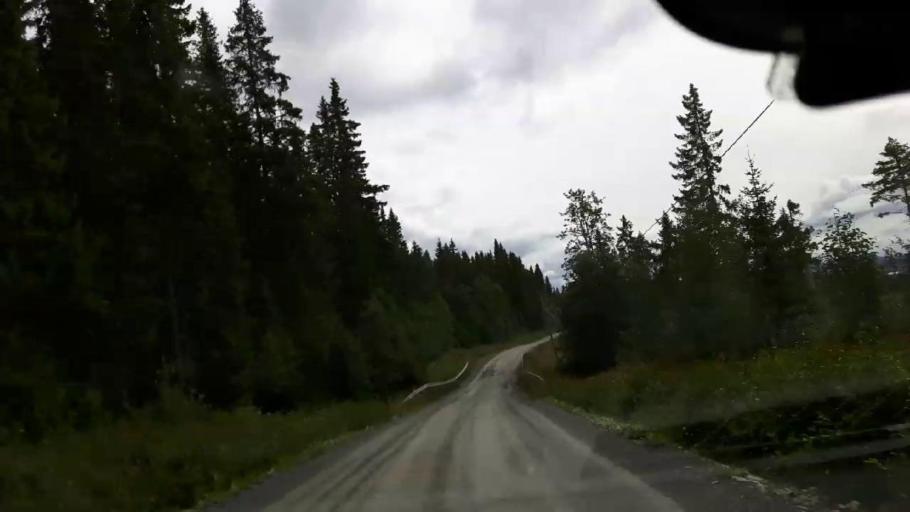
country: SE
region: Jaemtland
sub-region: Krokoms Kommun
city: Valla
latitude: 63.6785
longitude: 13.9313
